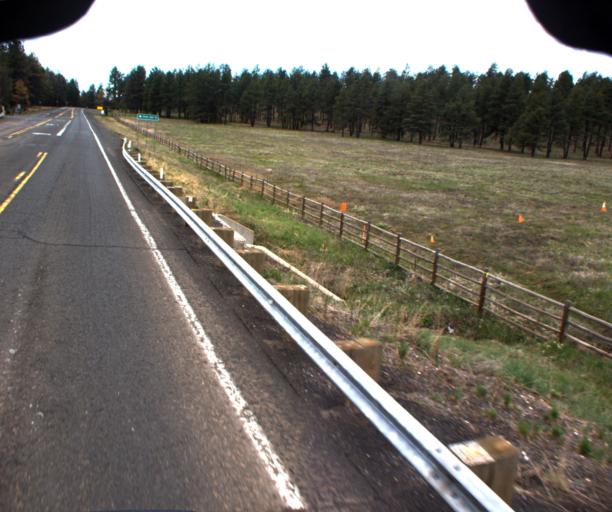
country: US
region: Arizona
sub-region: Coconino County
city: Kachina Village
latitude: 35.1289
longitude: -111.6909
